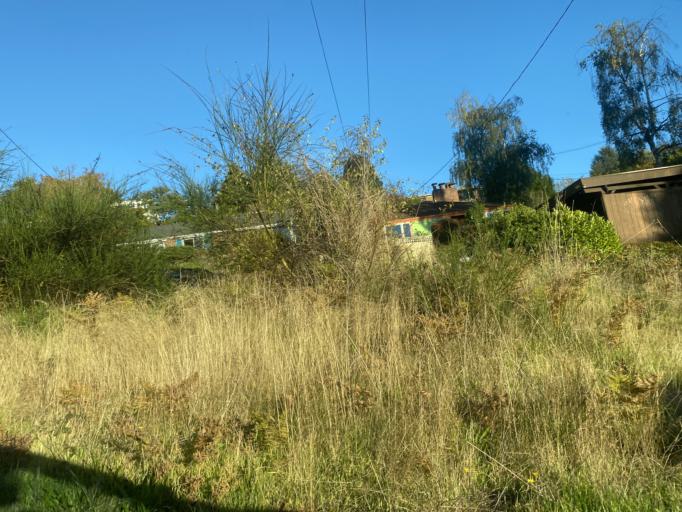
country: US
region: Washington
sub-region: King County
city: Seattle
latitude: 47.6473
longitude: -122.3957
